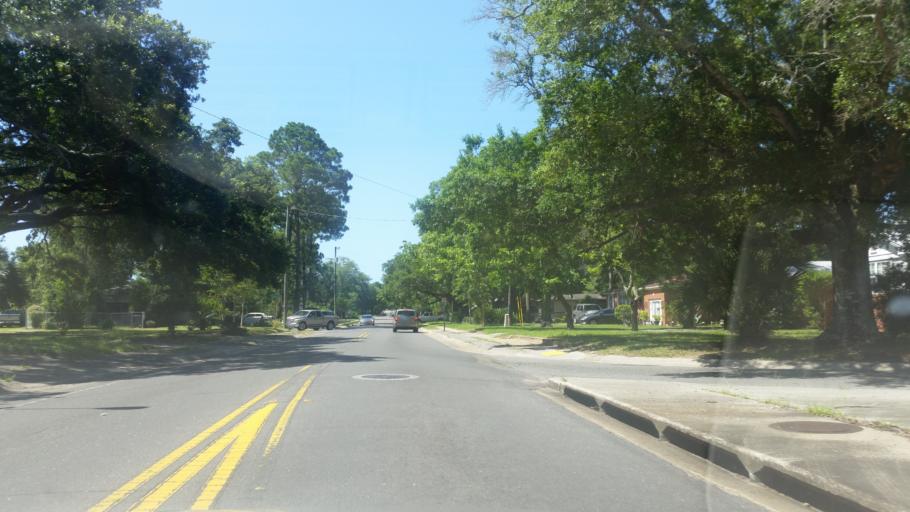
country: US
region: Florida
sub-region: Escambia County
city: Goulding
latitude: 30.4335
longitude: -87.2248
